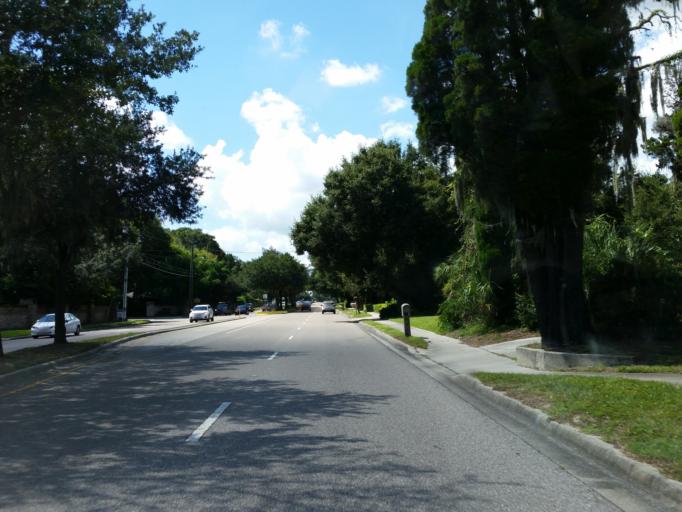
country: US
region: Florida
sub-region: Hillsborough County
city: Brandon
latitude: 27.9233
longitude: -82.2820
